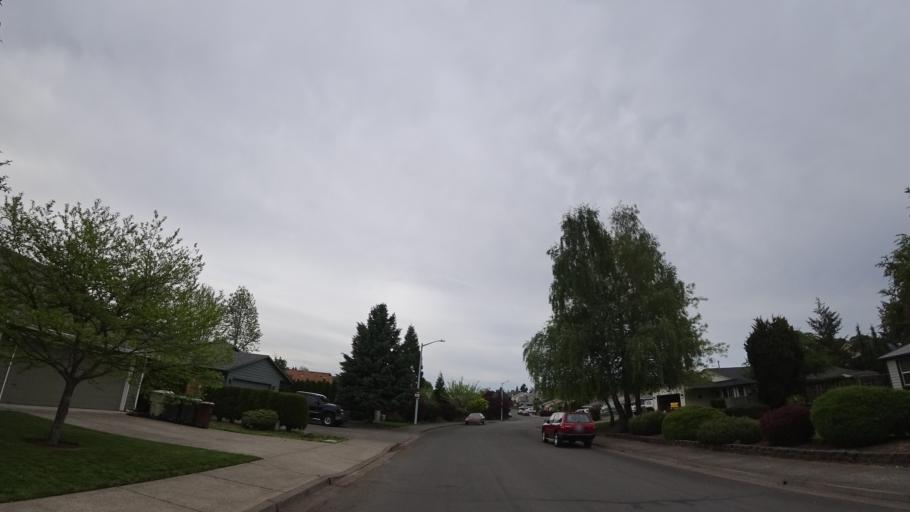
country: US
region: Oregon
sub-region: Washington County
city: Aloha
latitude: 45.5088
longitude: -122.9118
